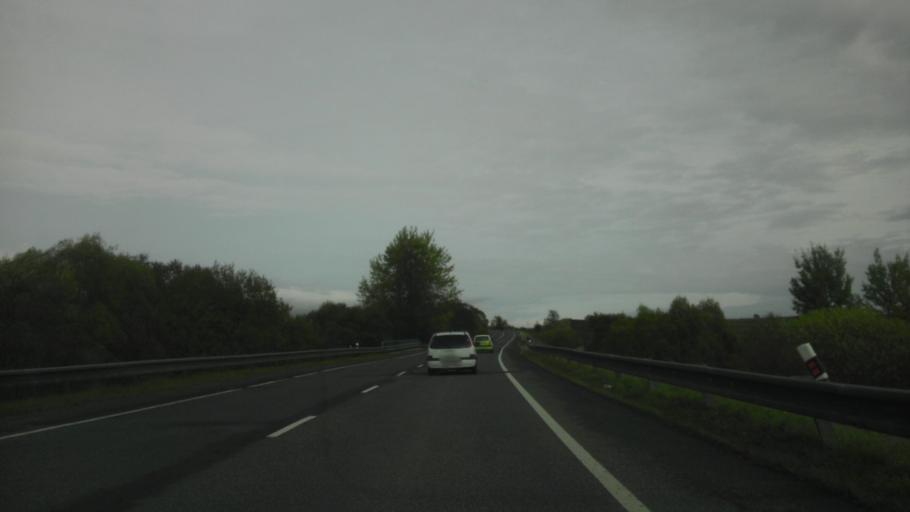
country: SK
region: Presovsky
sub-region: Okres Poprad
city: Nova Lesna
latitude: 49.1072
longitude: 20.2609
